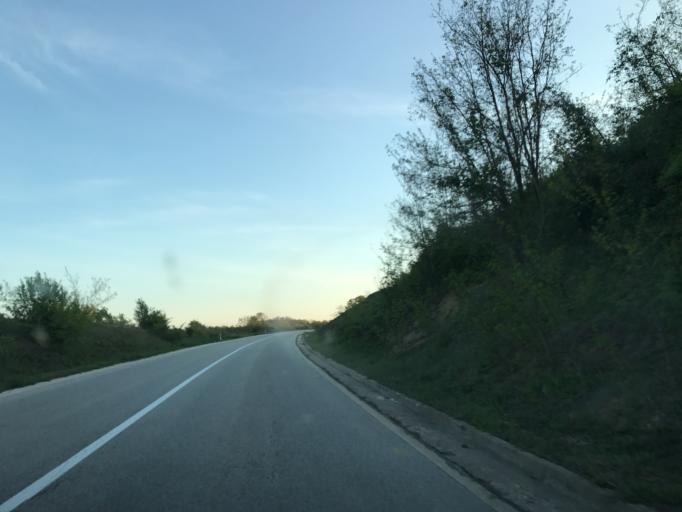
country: RO
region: Mehedinti
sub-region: Comuna Gogosu
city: Ostrovu Mare
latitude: 44.4108
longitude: 22.4846
